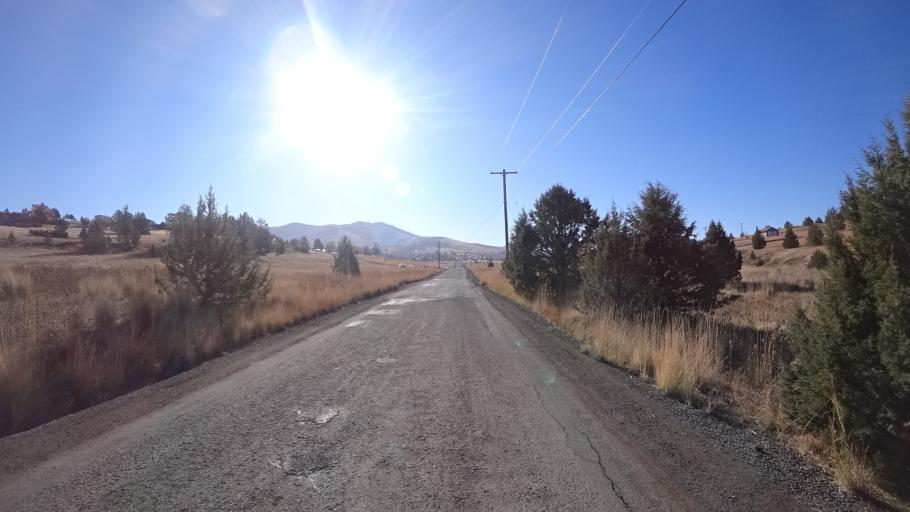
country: US
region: California
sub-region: Siskiyou County
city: Montague
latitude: 41.8846
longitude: -122.4261
